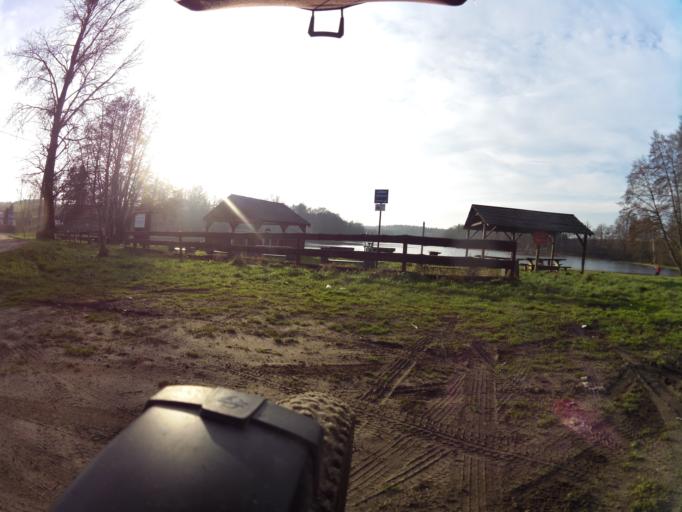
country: PL
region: West Pomeranian Voivodeship
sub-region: Powiat koszalinski
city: Polanow
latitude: 54.1564
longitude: 16.7313
